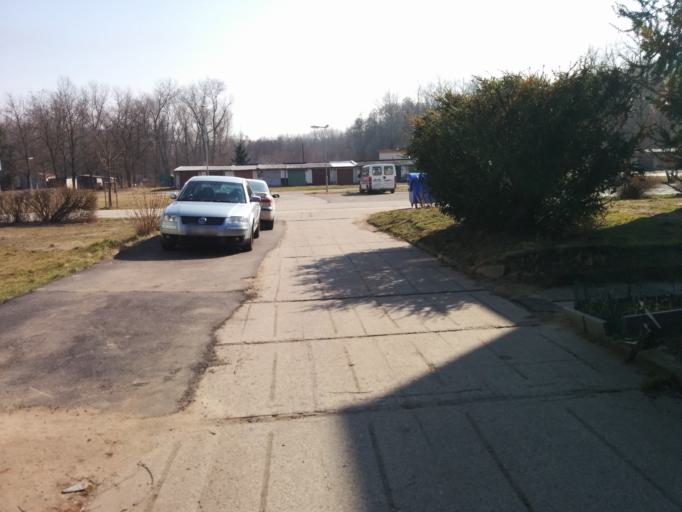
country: CZ
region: Central Bohemia
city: Libis
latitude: 50.2757
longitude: 14.5060
